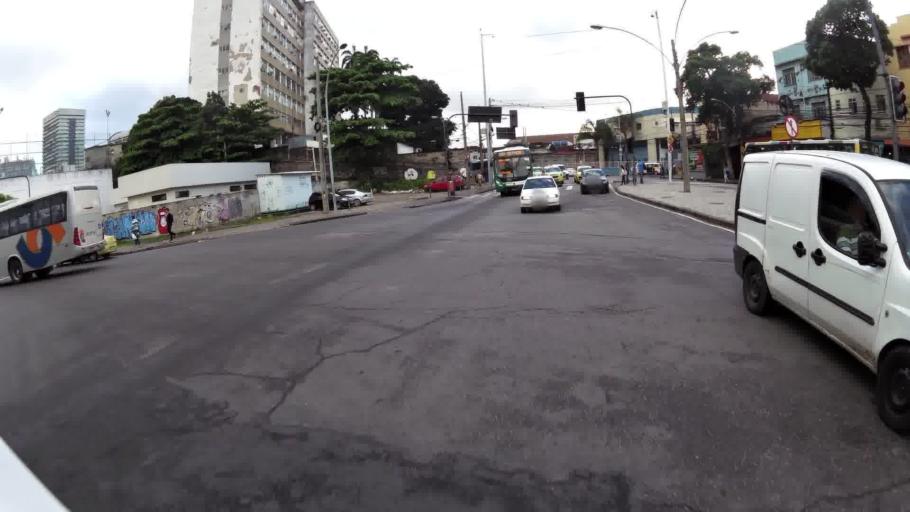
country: BR
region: Rio de Janeiro
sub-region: Rio De Janeiro
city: Rio de Janeiro
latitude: -22.9140
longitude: -43.2047
